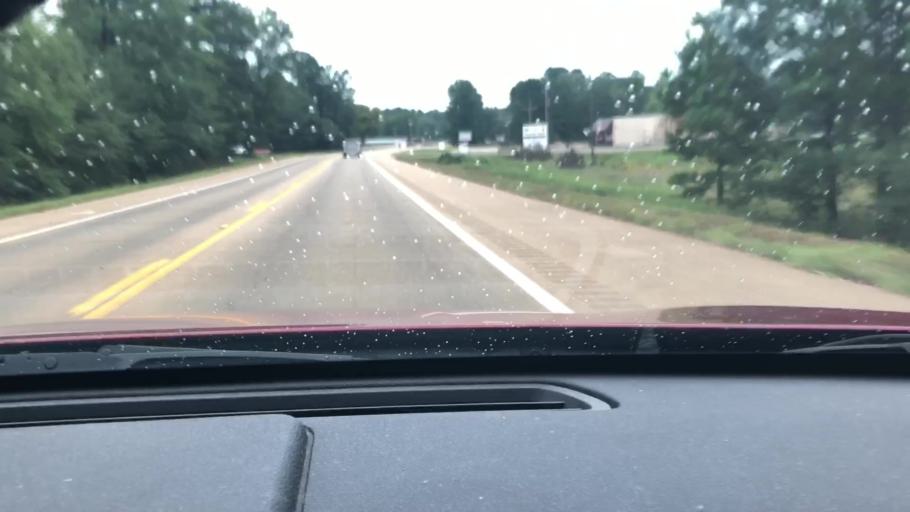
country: US
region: Arkansas
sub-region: Lafayette County
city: Stamps
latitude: 33.3674
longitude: -93.5176
